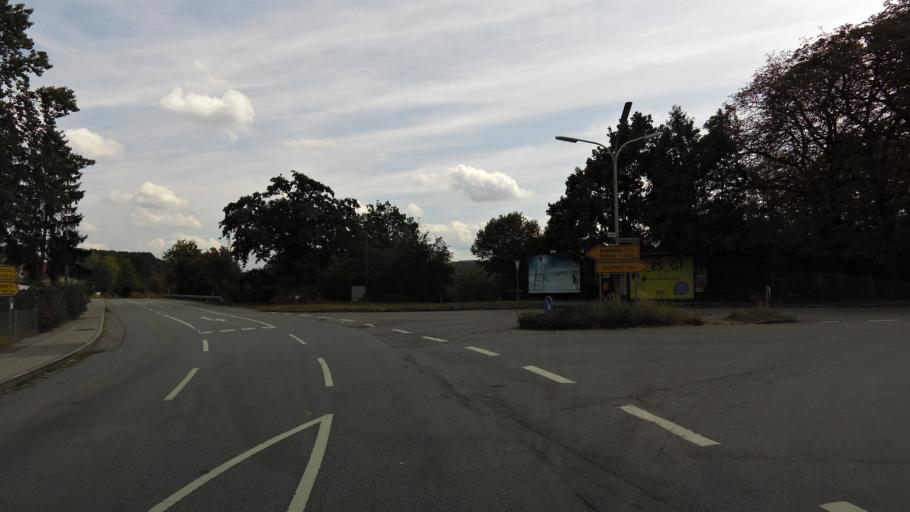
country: DE
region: Bavaria
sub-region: Upper Bavaria
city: Unterneukirchen
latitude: 48.1462
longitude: 12.6208
